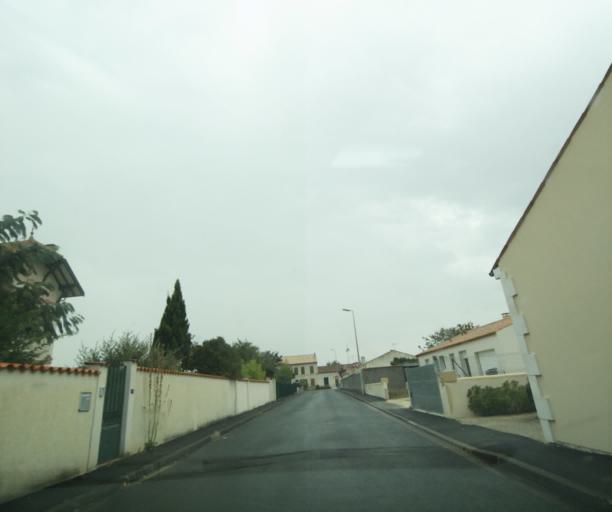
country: FR
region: Poitou-Charentes
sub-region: Departement de la Charente-Maritime
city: Tonnay-Charente
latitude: 45.9458
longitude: -0.9033
